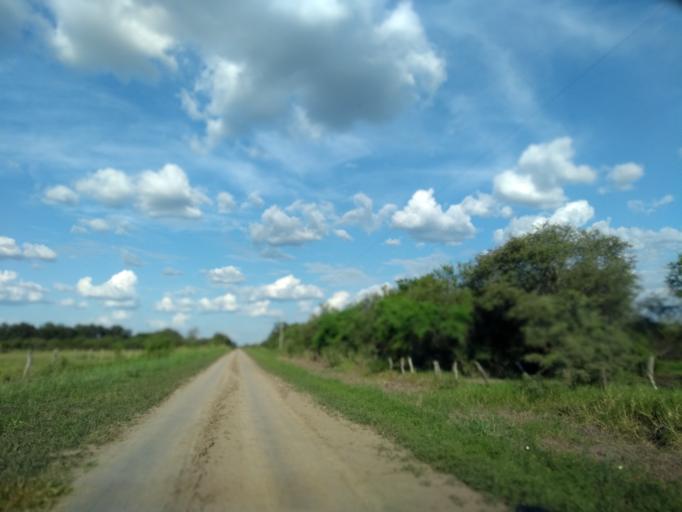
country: AR
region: Chaco
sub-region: Departamento de Quitilipi
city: Quitilipi
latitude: -26.7728
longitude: -60.1985
